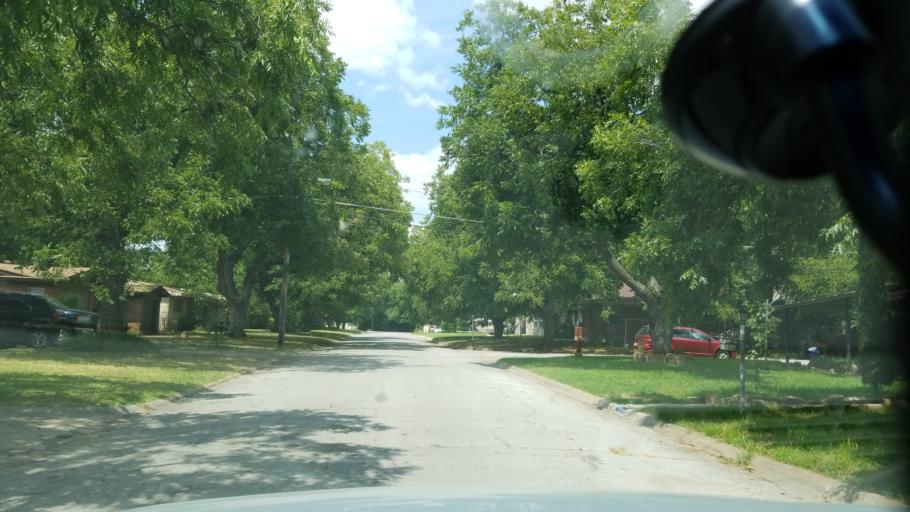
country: US
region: Texas
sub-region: Dallas County
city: Grand Prairie
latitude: 32.7543
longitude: -96.9887
